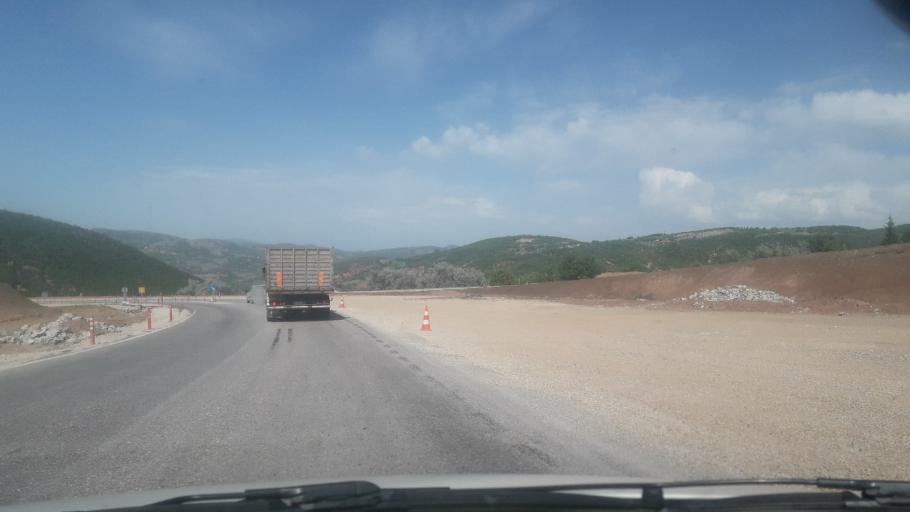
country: TR
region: Tokat
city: Tokat
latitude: 40.2075
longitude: 36.4985
